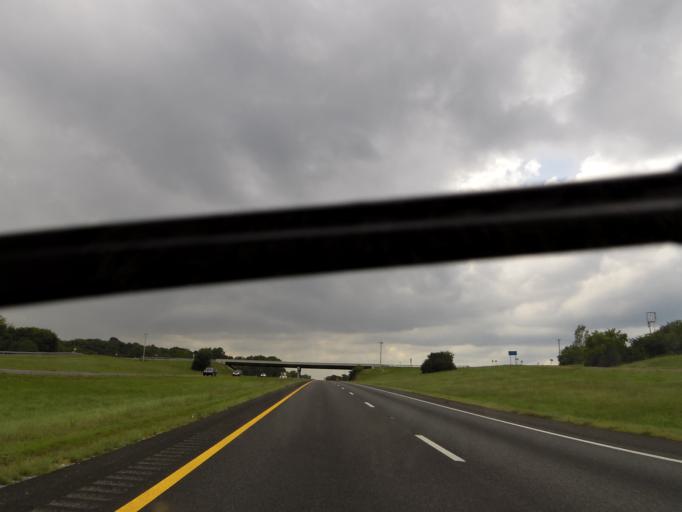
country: US
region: Tennessee
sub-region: Wilson County
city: Watertown
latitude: 36.1904
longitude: -86.1745
